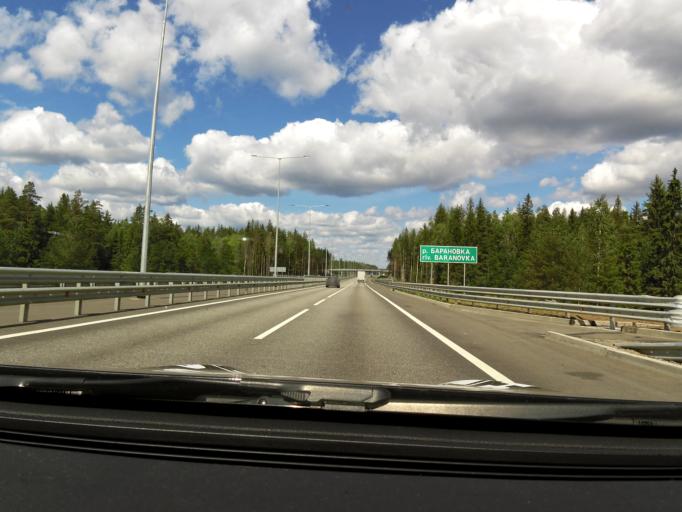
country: RU
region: Tverskaya
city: Krasnomayskiy
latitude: 57.4944
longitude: 34.3049
